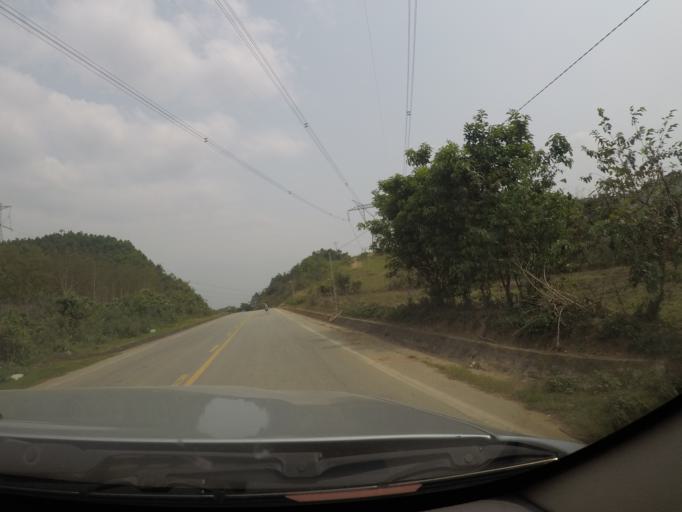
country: VN
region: Thanh Hoa
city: Thi Tran Yen Cat
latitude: 19.4761
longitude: 105.4158
